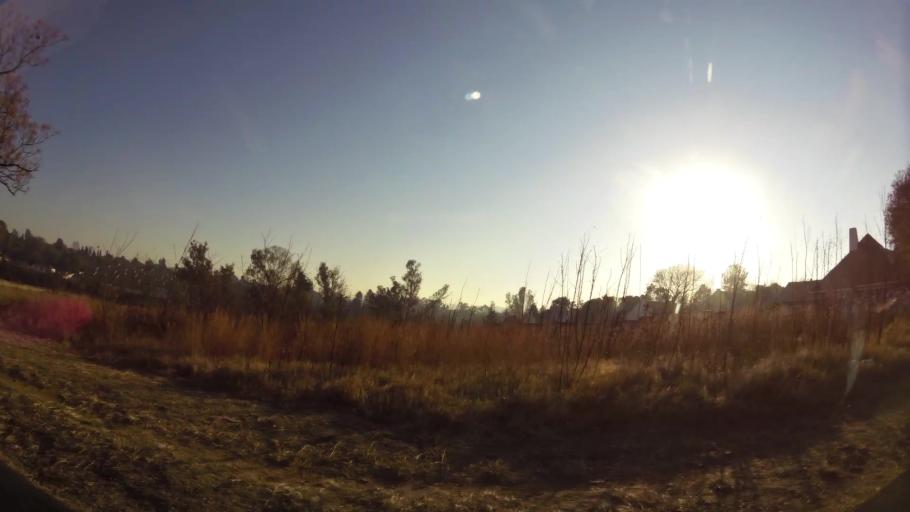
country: ZA
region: Gauteng
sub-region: City of Johannesburg Metropolitan Municipality
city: Midrand
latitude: -26.0511
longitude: 28.1073
